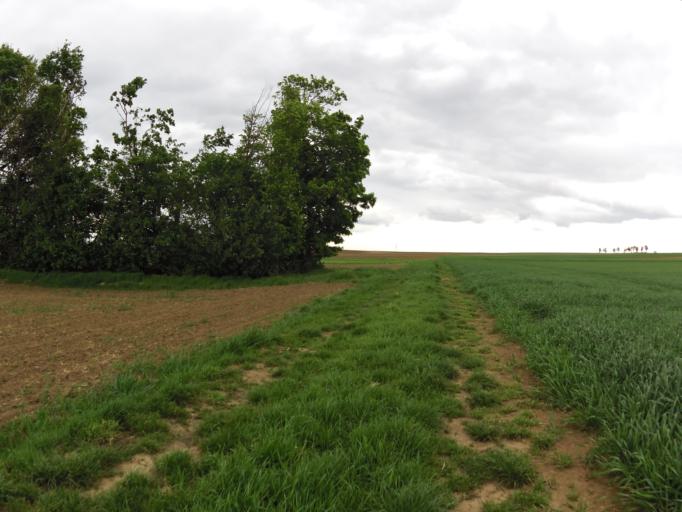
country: DE
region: Bavaria
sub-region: Regierungsbezirk Unterfranken
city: Unterpleichfeld
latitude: 49.8540
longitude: 10.0681
